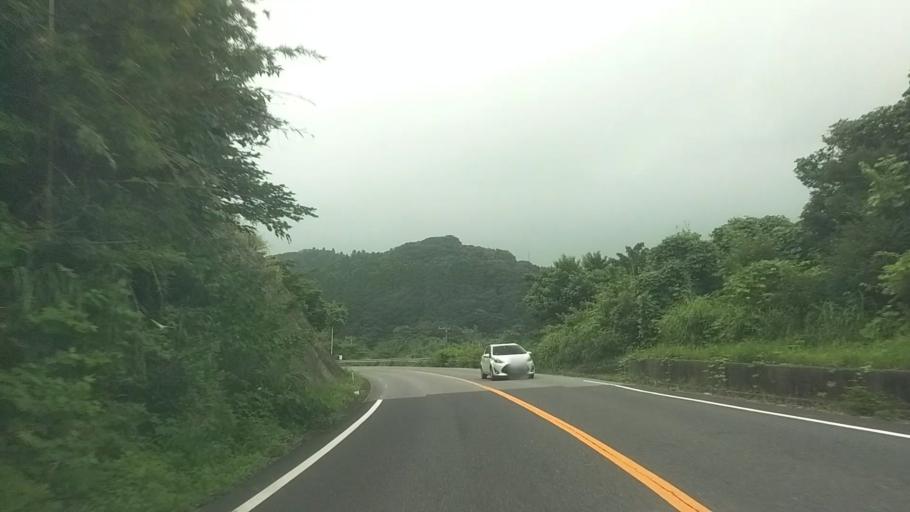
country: JP
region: Chiba
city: Katsuura
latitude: 35.1666
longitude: 140.3252
